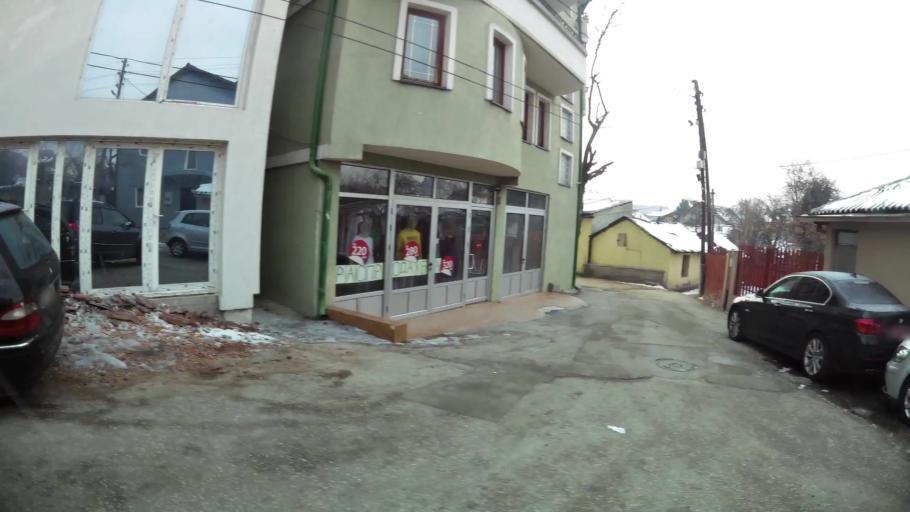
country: MK
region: Cair
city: Cair
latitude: 42.0146
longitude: 21.4412
